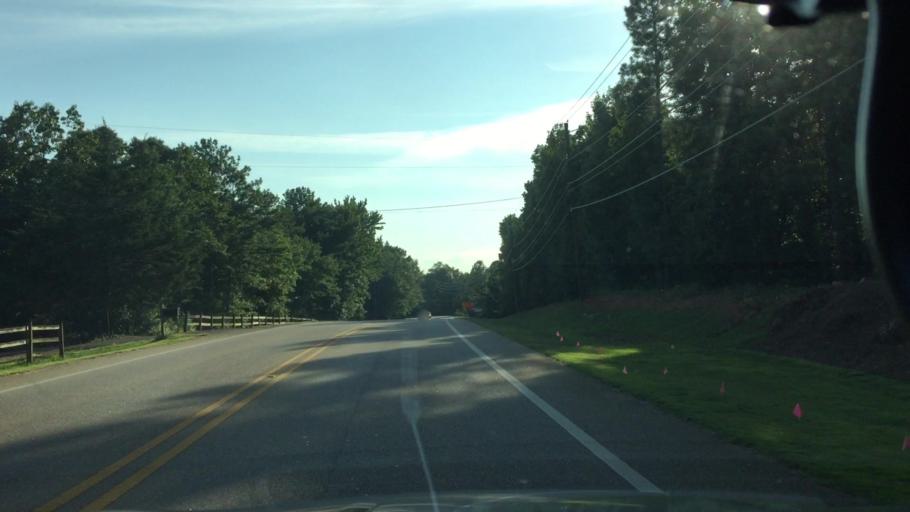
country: US
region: Alabama
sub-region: Lee County
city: Auburn
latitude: 32.5950
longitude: -85.4279
